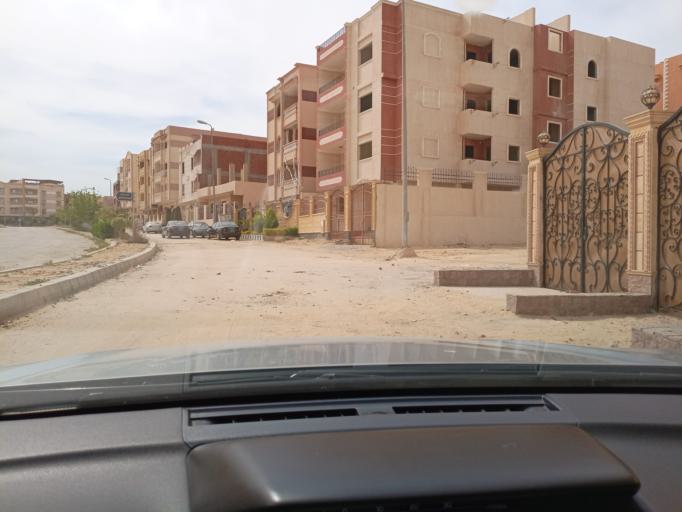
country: EG
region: Muhafazat al Qalyubiyah
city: Al Khankah
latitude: 30.2445
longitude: 31.4921
